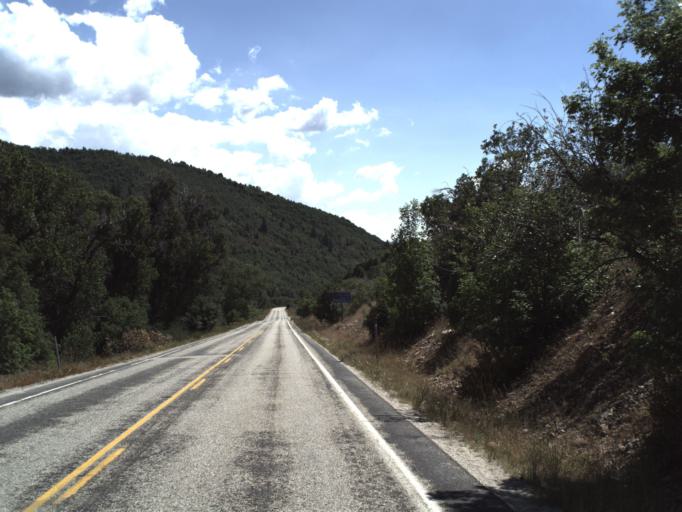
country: US
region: Utah
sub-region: Weber County
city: Wolf Creek
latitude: 41.3433
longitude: -111.6031
